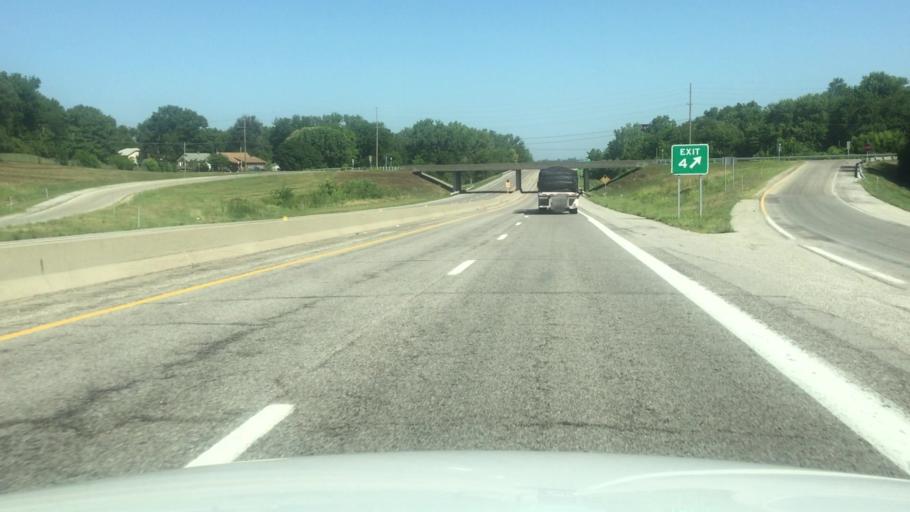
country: US
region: Kansas
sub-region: Doniphan County
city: Elwood
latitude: 39.7321
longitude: -94.8475
